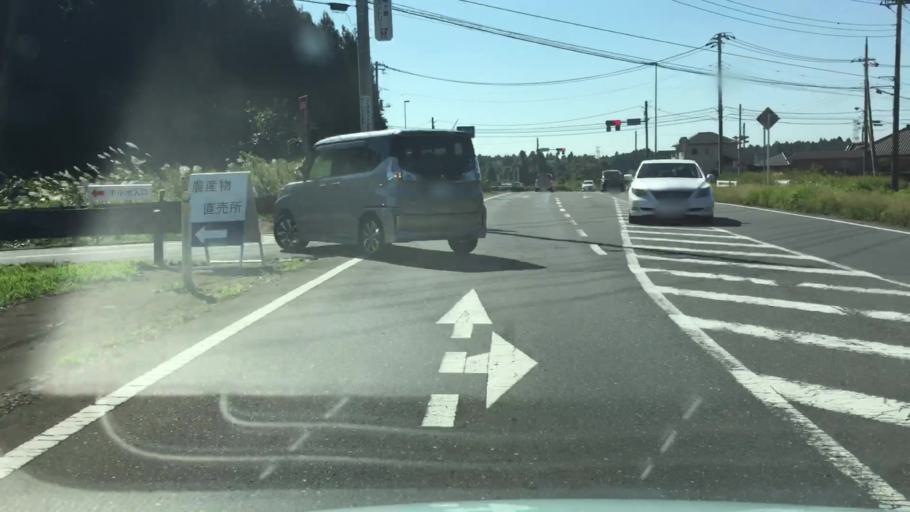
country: JP
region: Ibaraki
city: Ami
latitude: 35.9830
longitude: 140.1857
